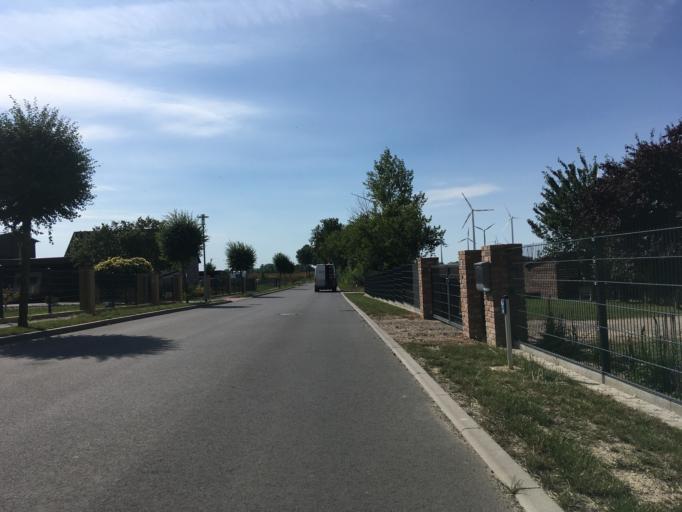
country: DE
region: Brandenburg
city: Gramzow
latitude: 53.2910
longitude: 14.0442
